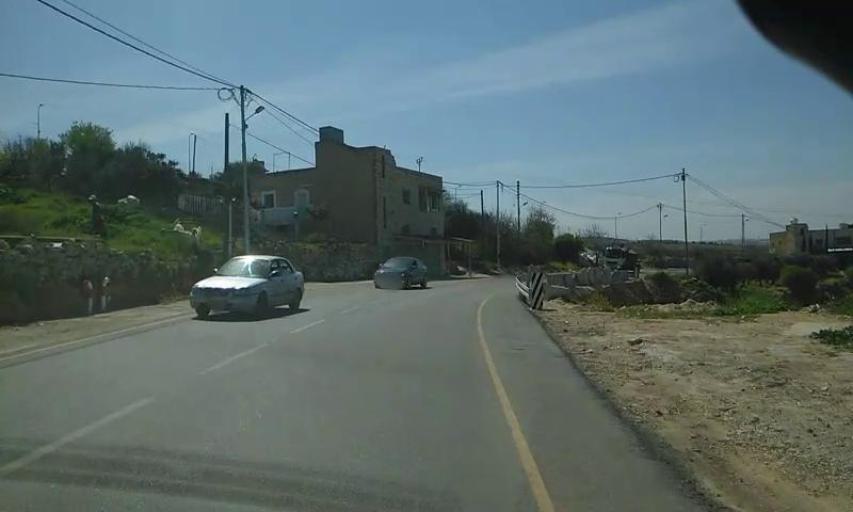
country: PS
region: West Bank
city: Husan
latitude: 31.7055
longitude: 35.1455
